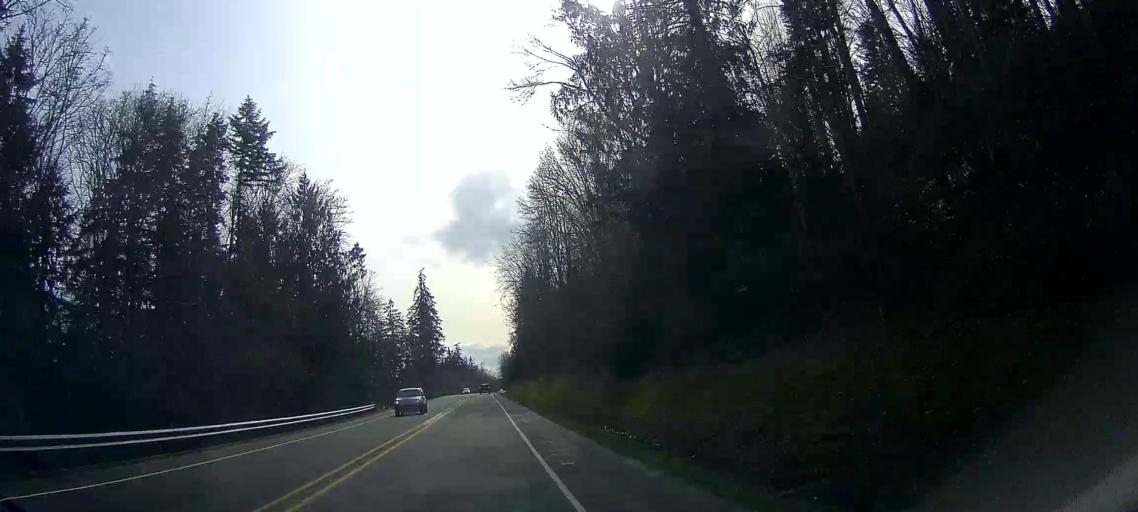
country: US
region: Washington
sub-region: Island County
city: Camano
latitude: 48.2035
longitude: -122.4791
